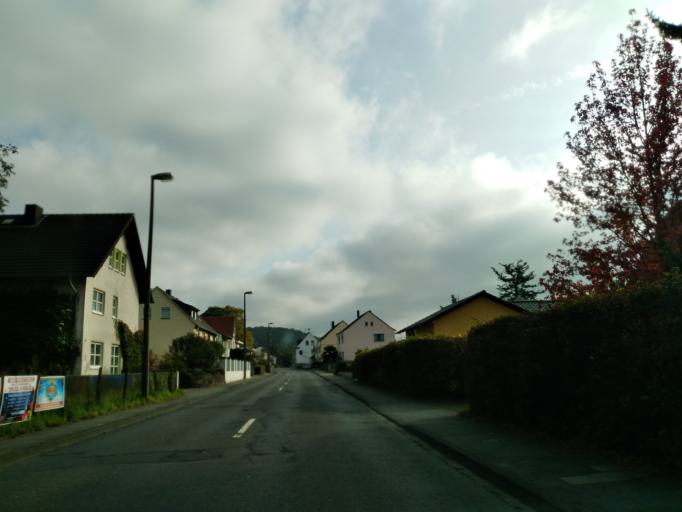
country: DE
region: North Rhine-Westphalia
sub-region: Regierungsbezirk Koln
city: Konigswinter
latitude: 50.7007
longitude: 7.1842
